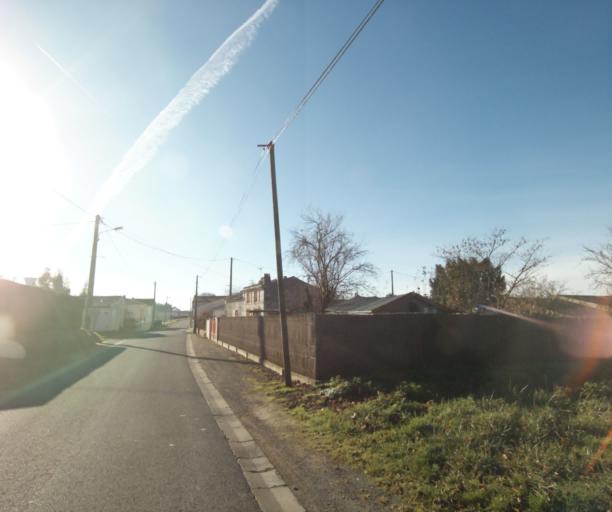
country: FR
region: Poitou-Charentes
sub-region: Departement de la Charente-Maritime
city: Fontcouverte
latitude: 45.7446
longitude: -0.5733
